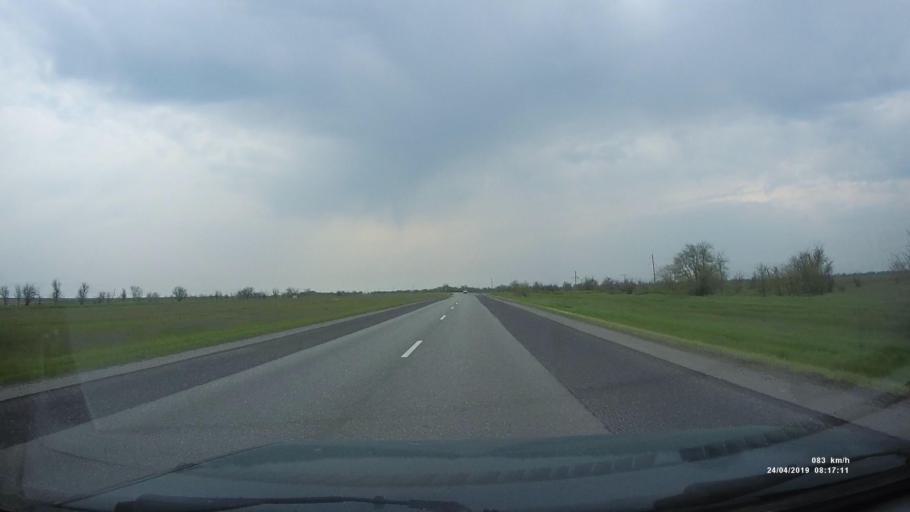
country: RU
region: Kalmykiya
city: Priyutnoye
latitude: 46.0981
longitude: 43.6254
